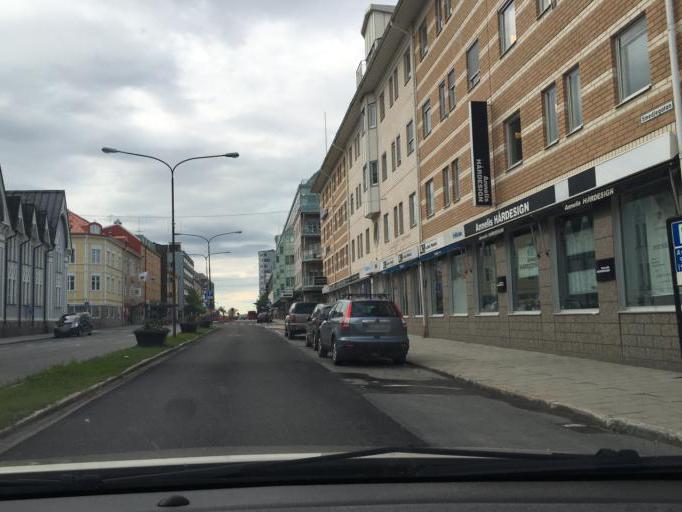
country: SE
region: Norrbotten
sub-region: Lulea Kommun
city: Lulea
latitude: 65.5822
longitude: 22.1535
